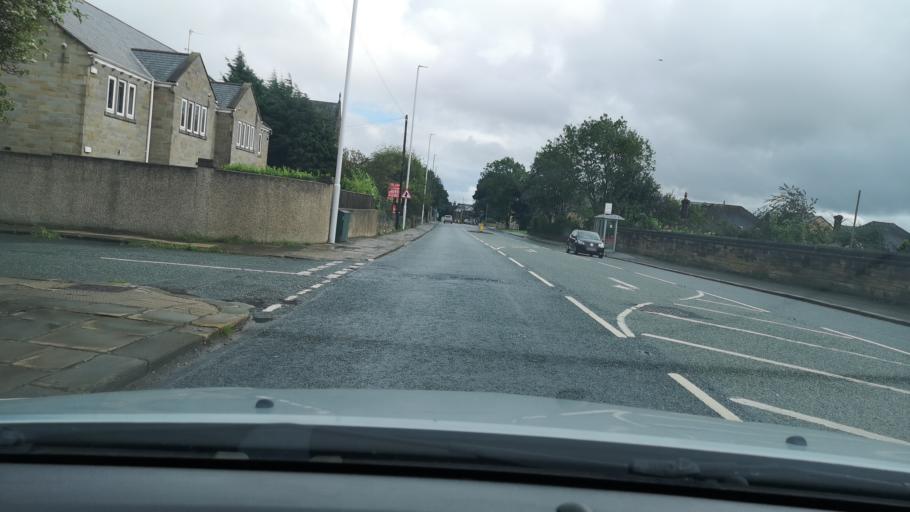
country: GB
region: England
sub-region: City and Borough of Leeds
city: Morley
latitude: 53.7399
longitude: -1.6175
